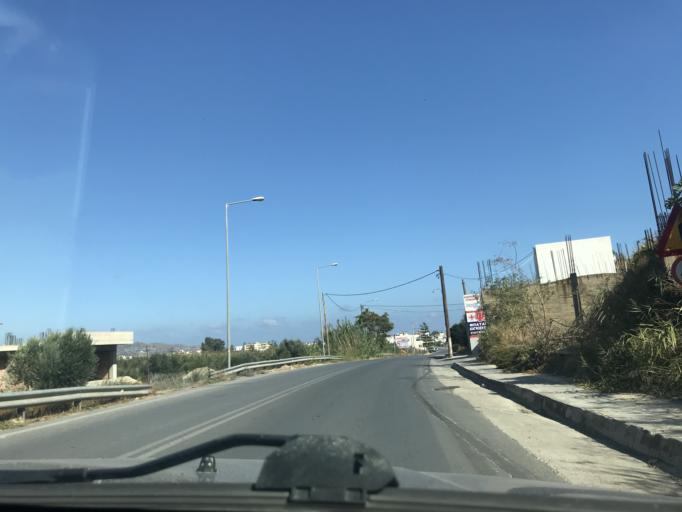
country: GR
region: Crete
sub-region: Nomos Irakleiou
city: Gazi
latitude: 35.3268
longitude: 25.0637
